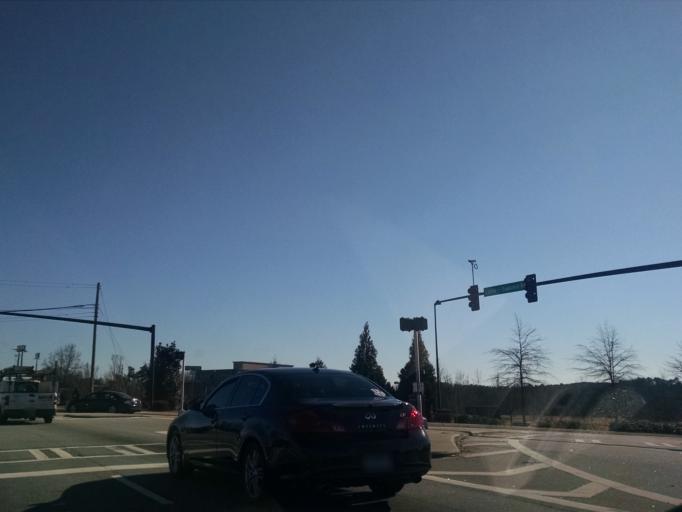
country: US
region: Georgia
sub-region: Gwinnett County
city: Suwanee
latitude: 34.0343
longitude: -84.0517
